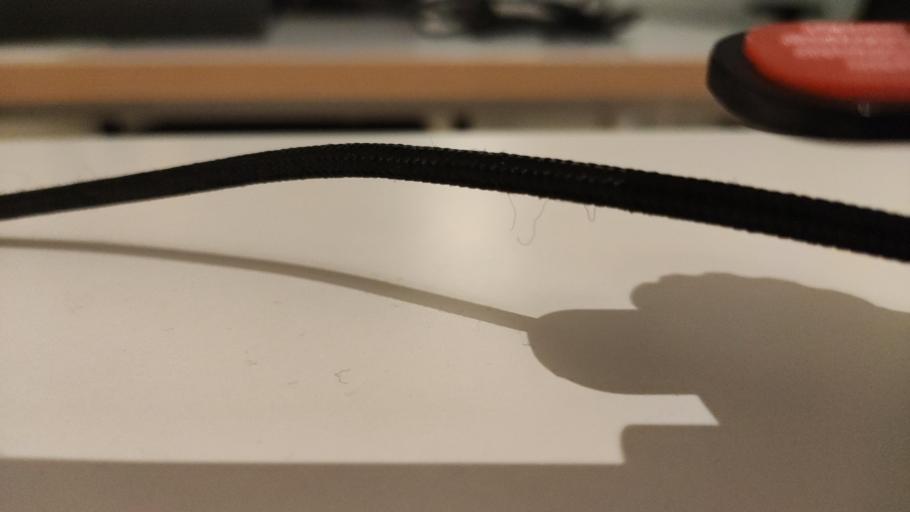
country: RU
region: Moskovskaya
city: Novoye
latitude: 55.6430
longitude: 38.9291
